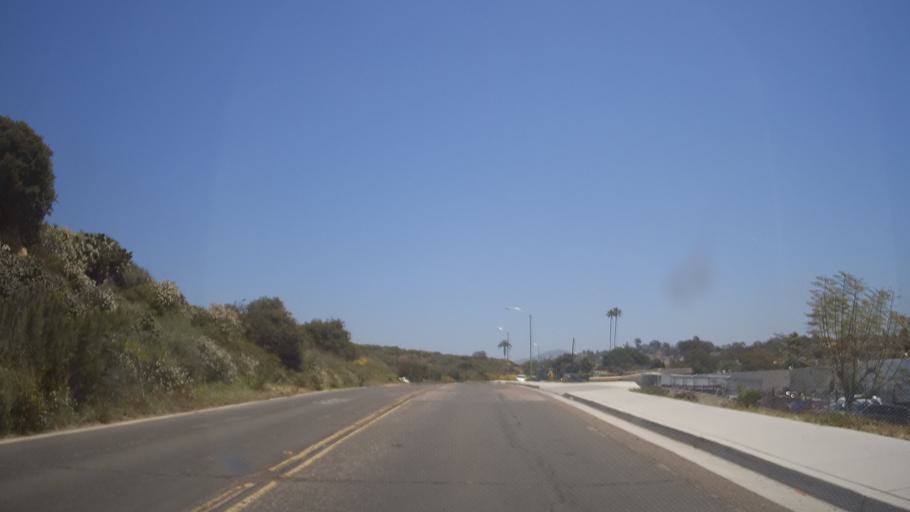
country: US
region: California
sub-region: San Diego County
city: National City
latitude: 32.7104
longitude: -117.0784
